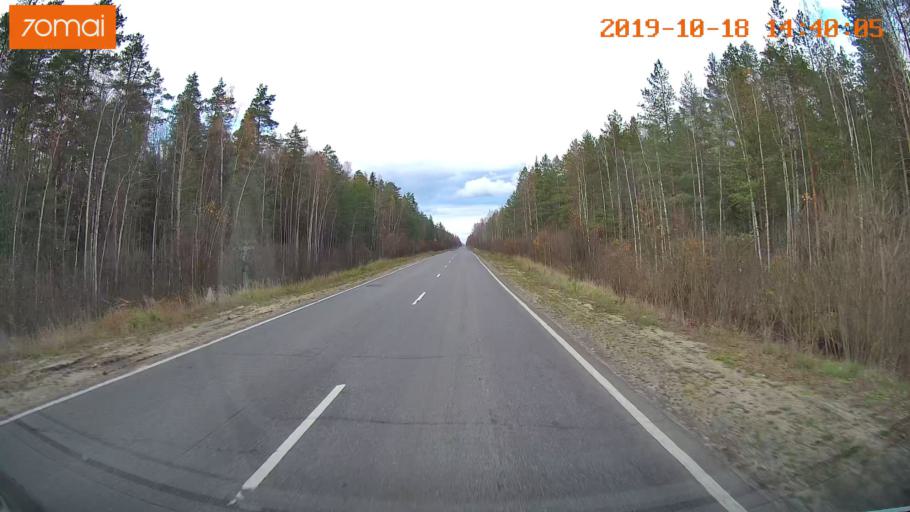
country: RU
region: Vladimir
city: Velikodvorskiy
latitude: 55.2713
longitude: 40.6683
